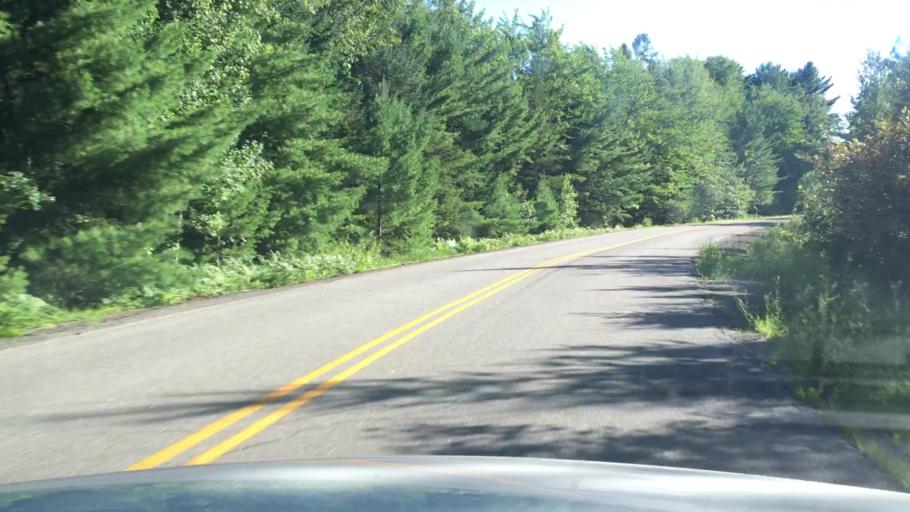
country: US
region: Maine
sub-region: Penobscot County
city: Enfield
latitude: 45.1917
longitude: -68.6073
